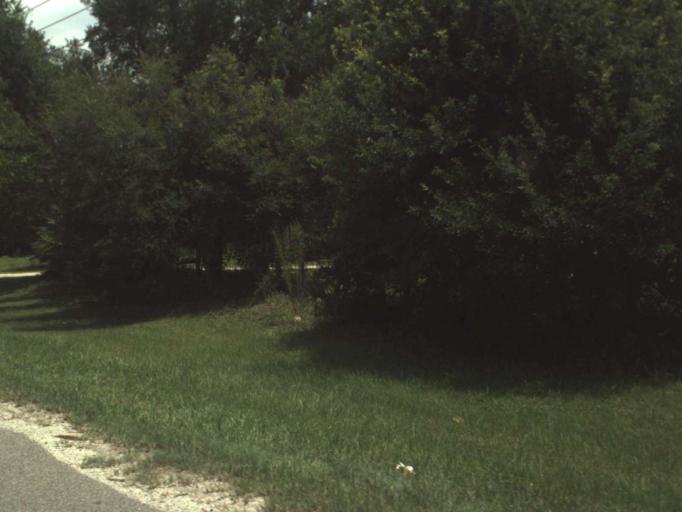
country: US
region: Florida
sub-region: Sumter County
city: Wildwood
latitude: 28.8138
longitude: -82.0456
